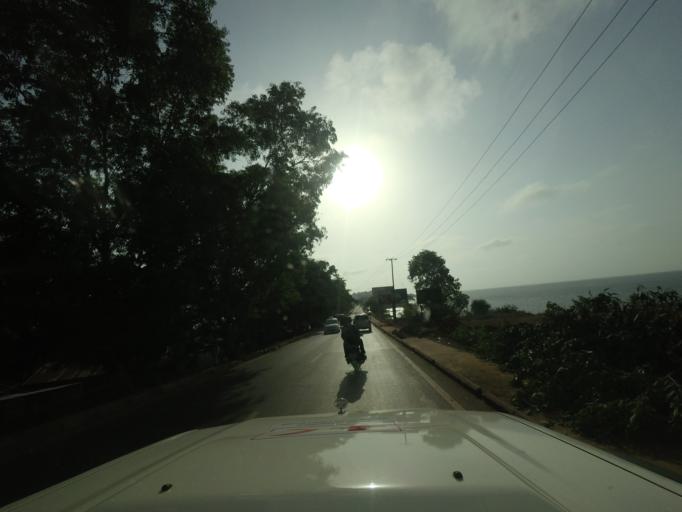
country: SL
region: Western Area
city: Freetown
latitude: 8.4920
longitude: -13.2708
